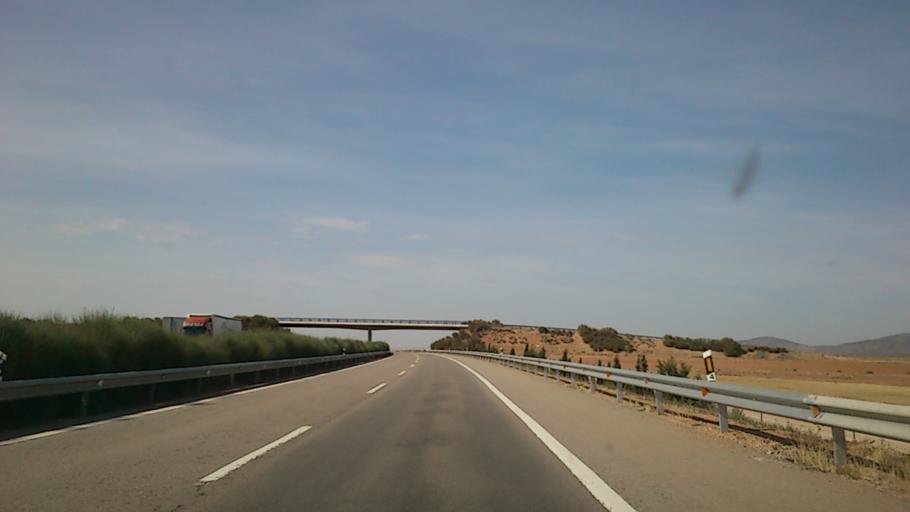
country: ES
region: Aragon
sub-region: Provincia de Teruel
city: Villarquemado
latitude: 40.5173
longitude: -1.2538
